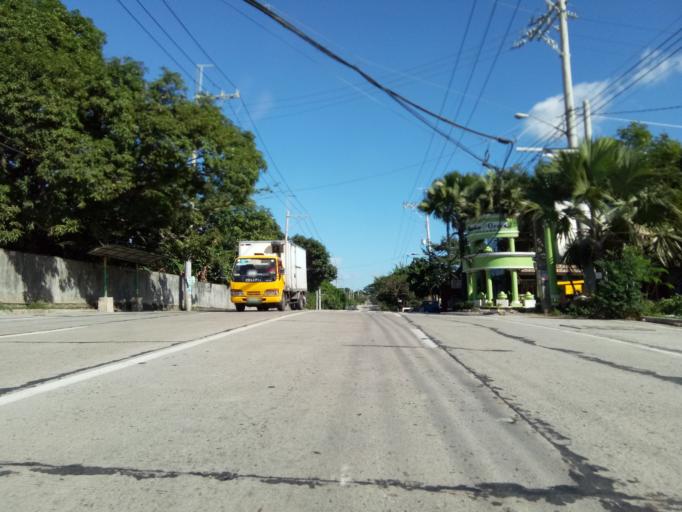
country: PH
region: Calabarzon
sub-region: Province of Cavite
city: Dasmarinas
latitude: 14.3518
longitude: 120.9517
